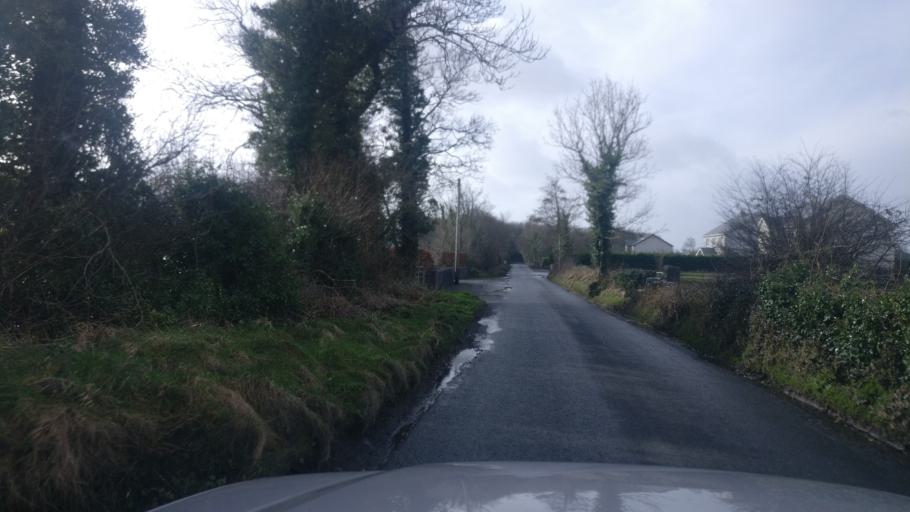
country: IE
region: Connaught
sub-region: County Galway
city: Loughrea
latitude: 53.2755
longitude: -8.5855
